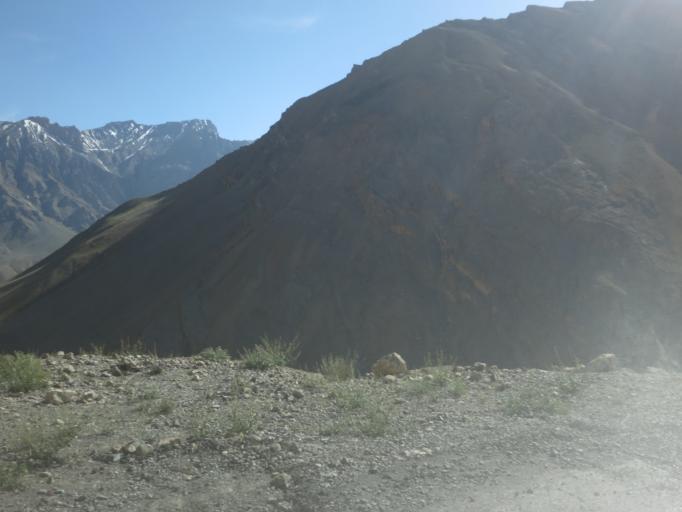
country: IN
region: Himachal Pradesh
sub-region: Kulu
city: Manali
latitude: 32.3235
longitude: 78.0023
